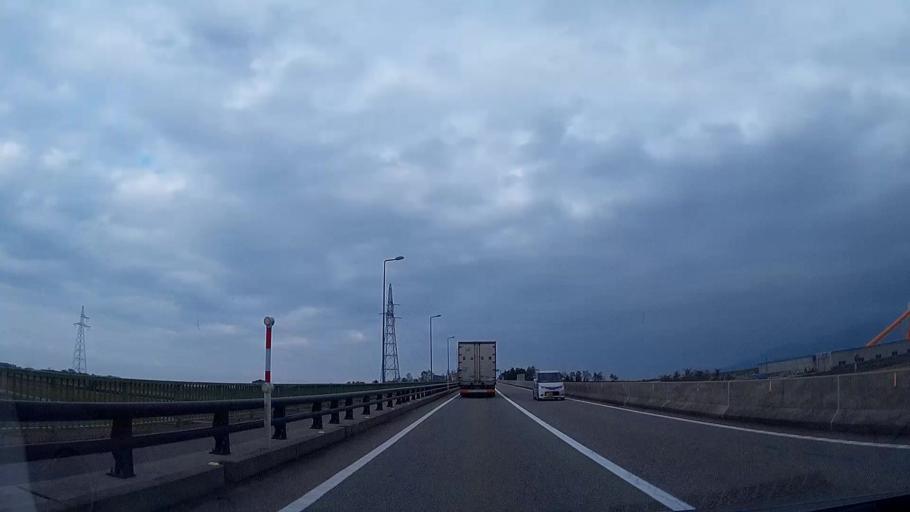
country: JP
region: Toyama
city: Nyuzen
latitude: 36.9008
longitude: 137.4468
